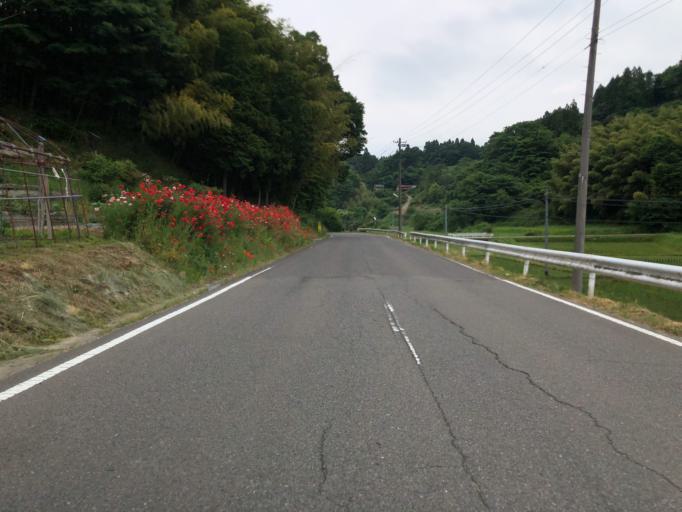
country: JP
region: Fukushima
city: Funehikimachi-funehiki
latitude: 37.4824
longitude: 140.5435
